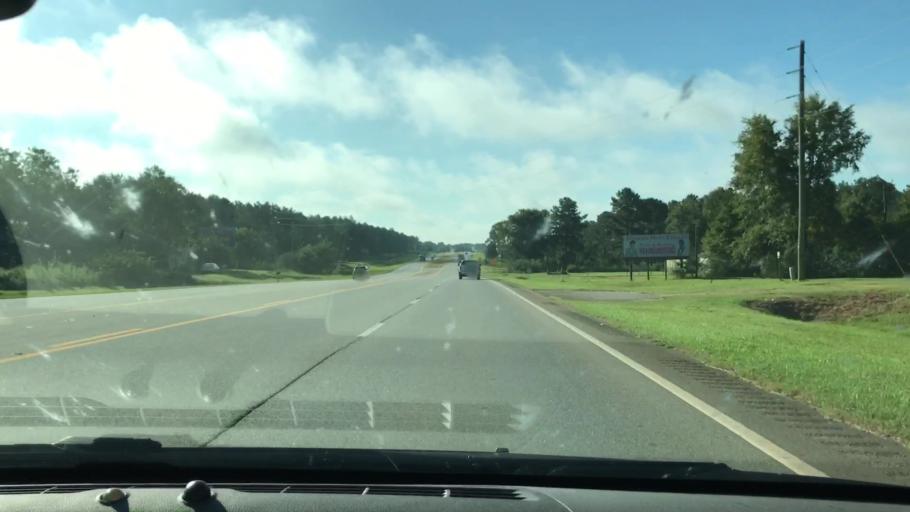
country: US
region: Georgia
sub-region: Terrell County
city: Dawson
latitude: 31.7525
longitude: -84.4234
